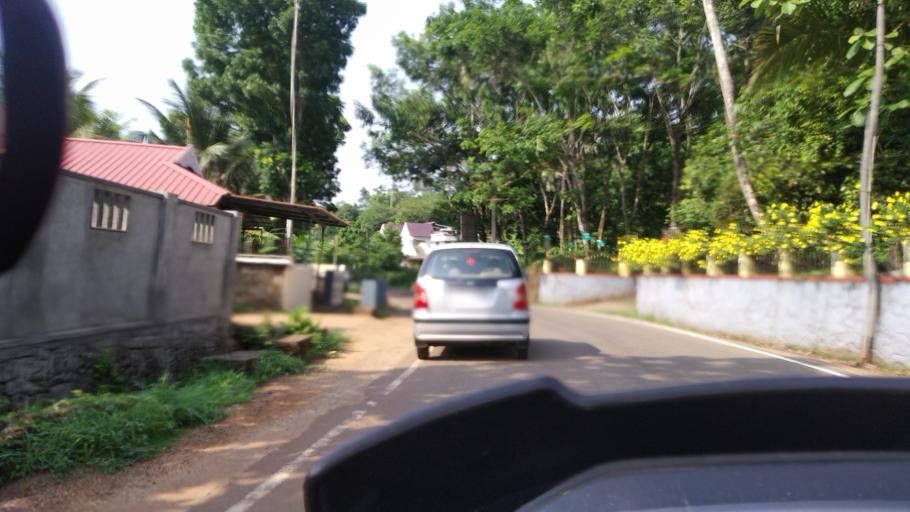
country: IN
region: Kerala
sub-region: Ernakulam
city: Piravam
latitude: 9.8418
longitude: 76.5355
